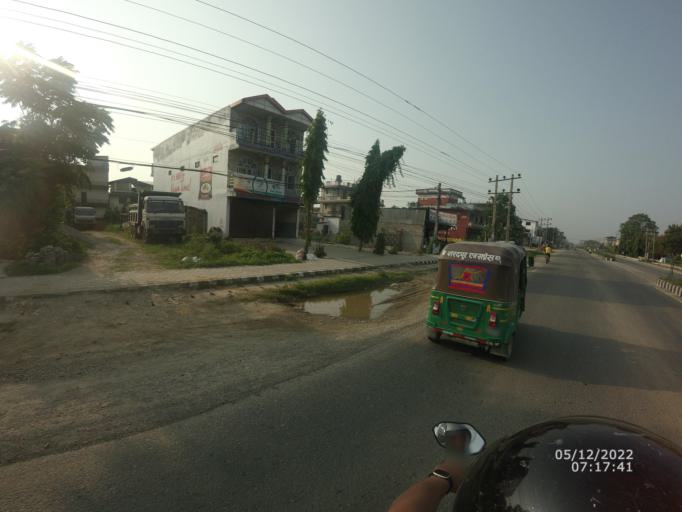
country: NP
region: Central Region
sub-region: Narayani Zone
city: Bharatpur
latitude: 27.6768
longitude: 84.4391
